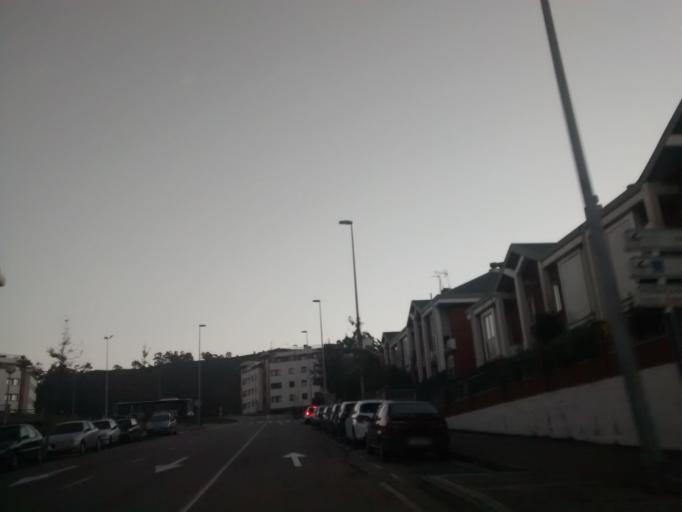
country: ES
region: Cantabria
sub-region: Provincia de Cantabria
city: Santa Cruz de Bezana
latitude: 43.4558
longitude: -3.8562
